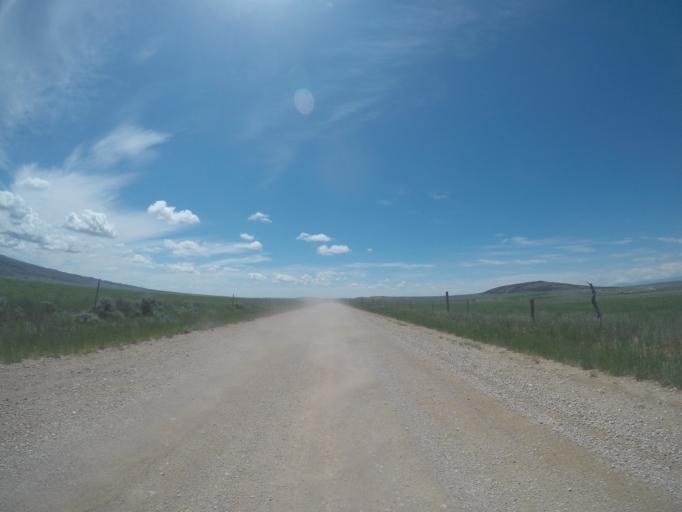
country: US
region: Wyoming
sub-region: Park County
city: Powell
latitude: 45.2113
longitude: -108.7190
